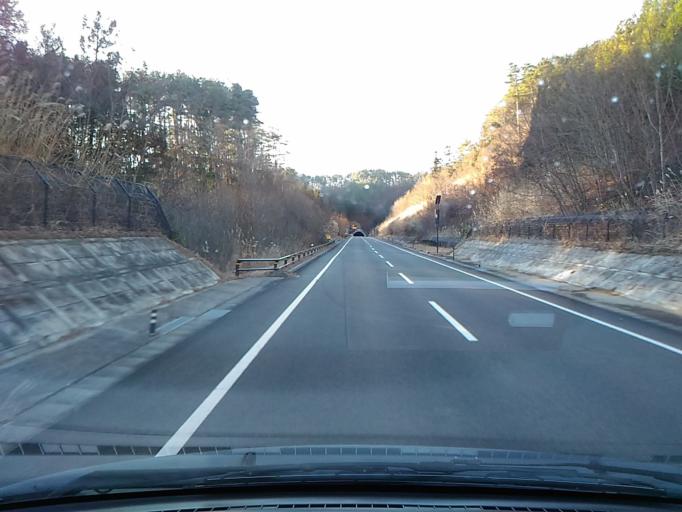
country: JP
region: Ibaraki
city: Kitaibaraki
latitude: 36.9719
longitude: 140.6076
